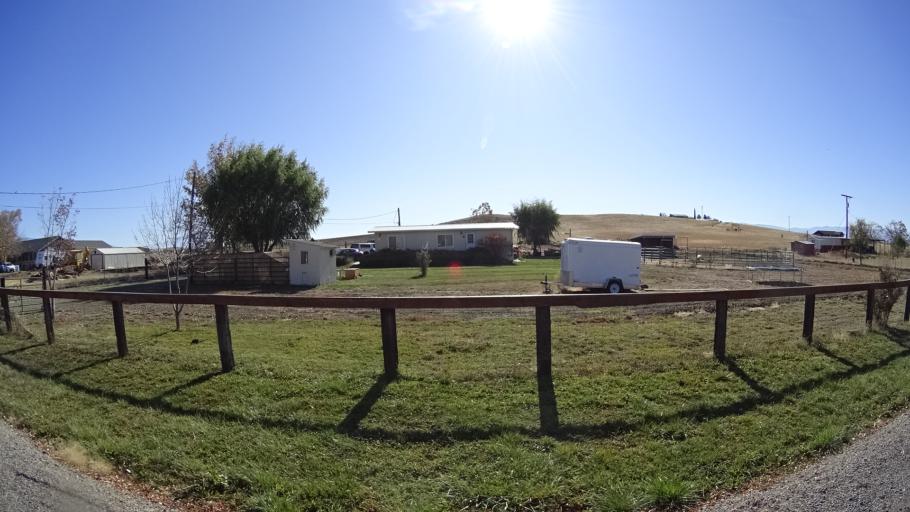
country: US
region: California
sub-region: Siskiyou County
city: Montague
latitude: 41.7558
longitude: -122.4663
